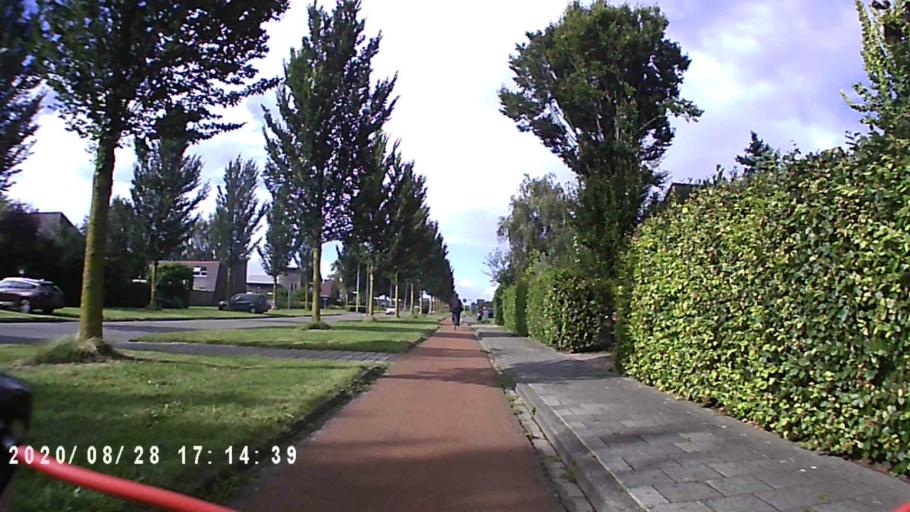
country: NL
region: Groningen
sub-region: Gemeente Groningen
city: Groningen
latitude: 53.2016
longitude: 6.5286
